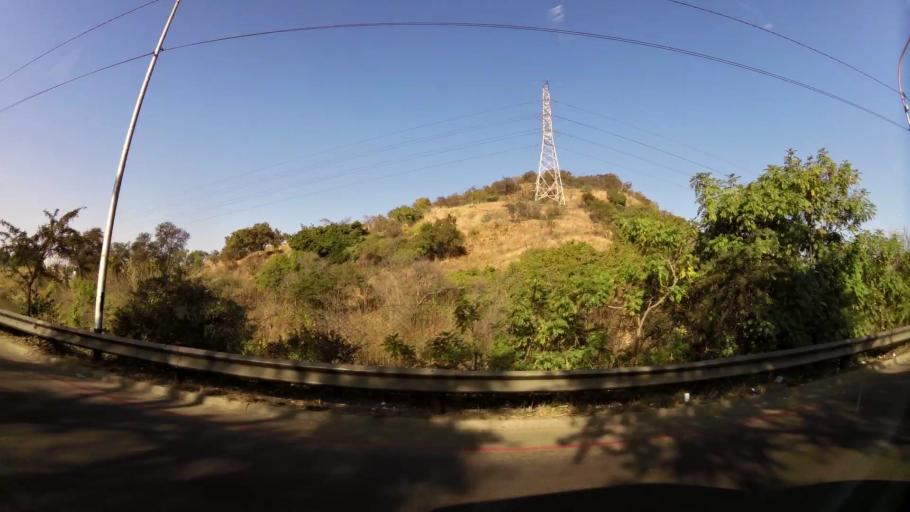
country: ZA
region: Gauteng
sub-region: City of Tshwane Metropolitan Municipality
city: Pretoria
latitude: -25.7283
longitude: 28.1698
